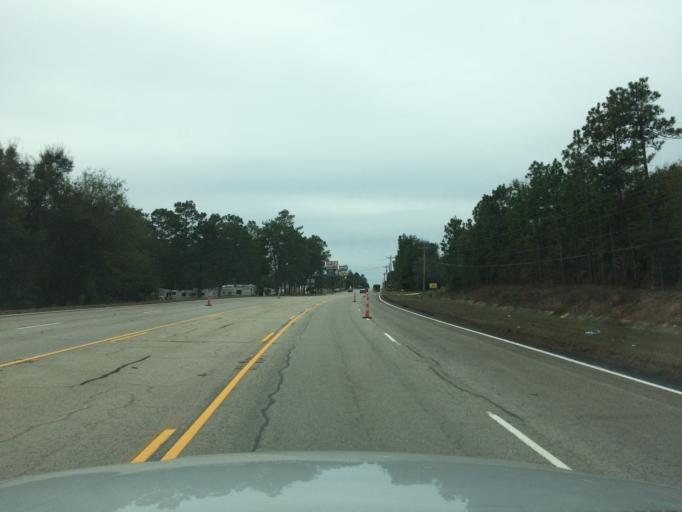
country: US
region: South Carolina
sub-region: Aiken County
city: Aiken
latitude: 33.6007
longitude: -81.6868
